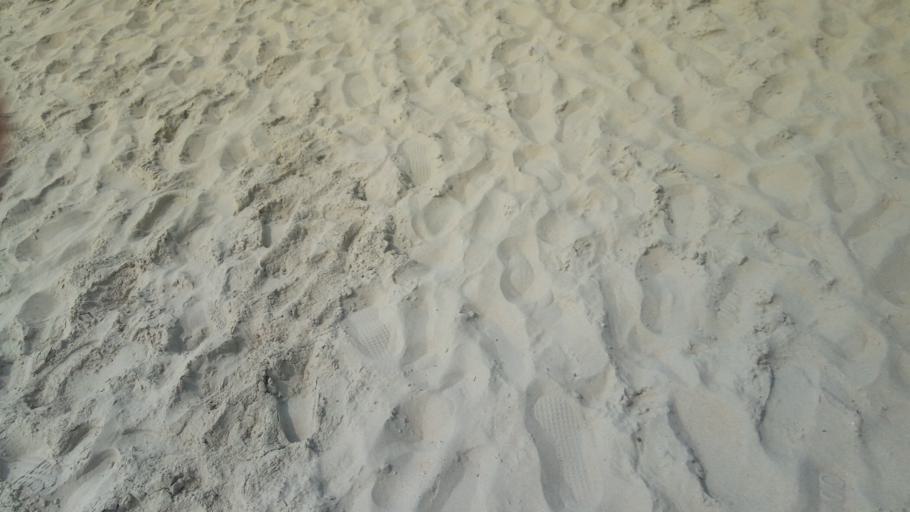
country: IN
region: Goa
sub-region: South Goa
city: Benaulim
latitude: 15.2574
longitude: 73.9191
